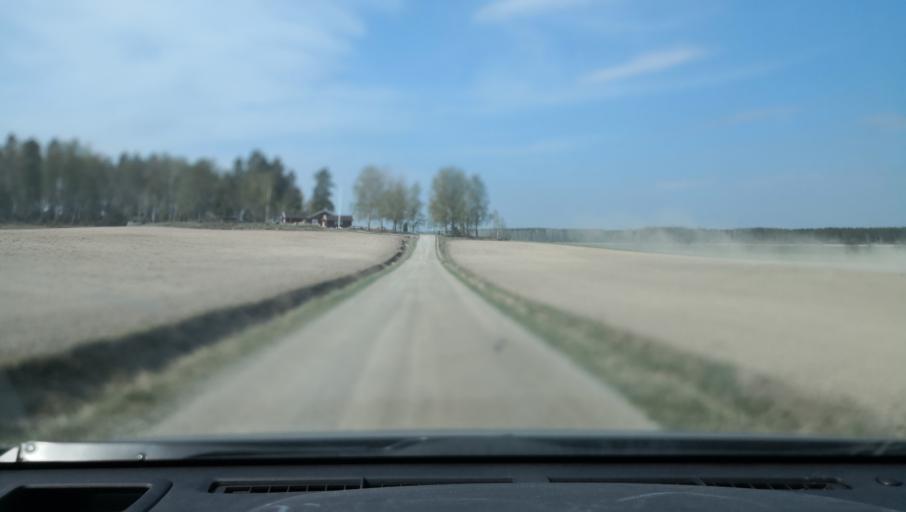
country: SE
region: Vaestmanland
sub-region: Vasteras
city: Skultuna
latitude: 59.7746
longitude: 16.4361
